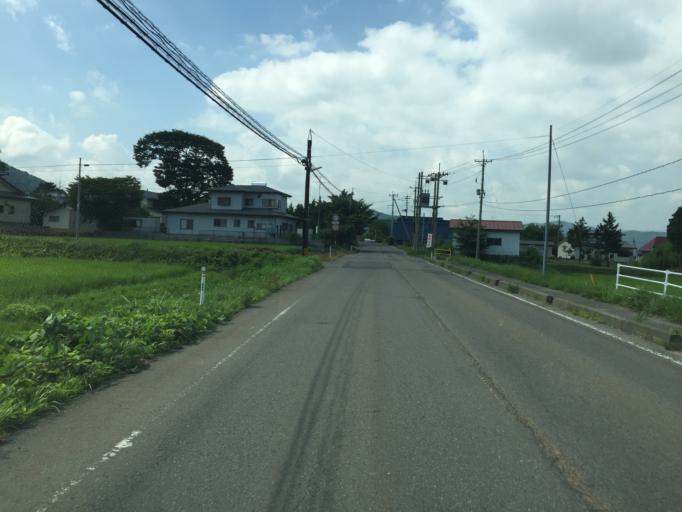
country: JP
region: Fukushima
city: Inawashiro
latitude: 37.4242
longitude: 140.1462
